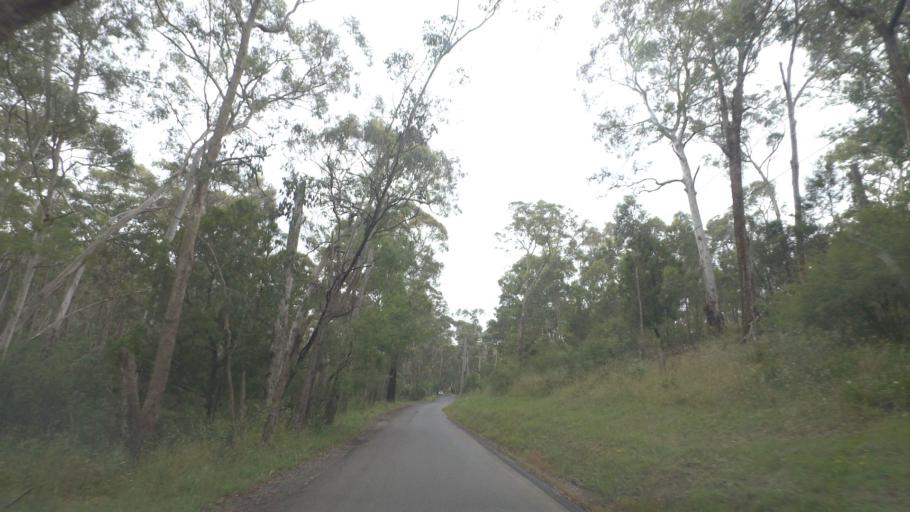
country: AU
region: Victoria
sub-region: Manningham
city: Warrandyte
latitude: -37.7508
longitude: 145.2197
